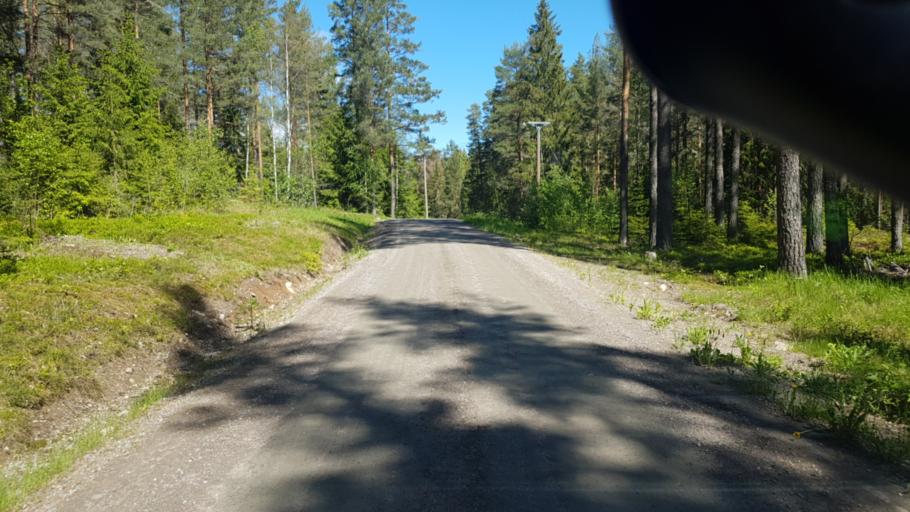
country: SE
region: Vaermland
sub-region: Grums Kommun
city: Grums
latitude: 59.4944
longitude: 12.9270
